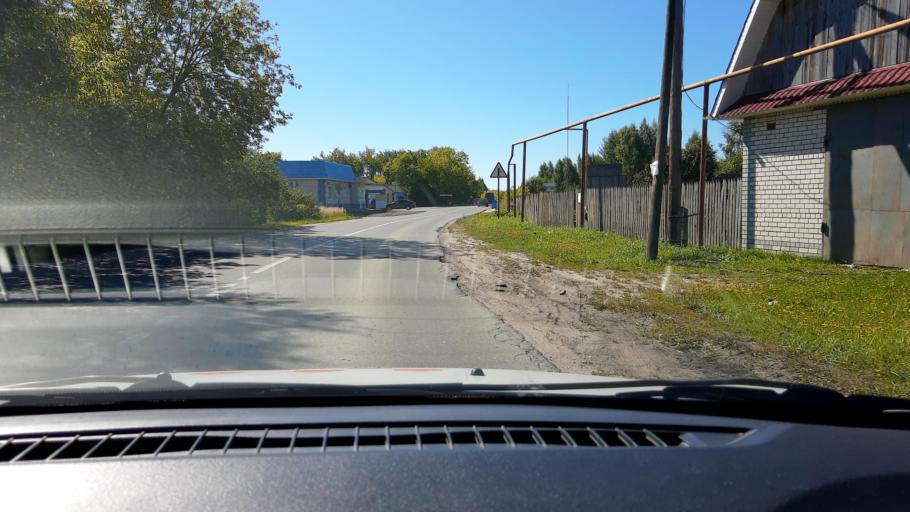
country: RU
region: Nizjnij Novgorod
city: Zavolzh'ye
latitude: 56.7120
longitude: 43.4160
